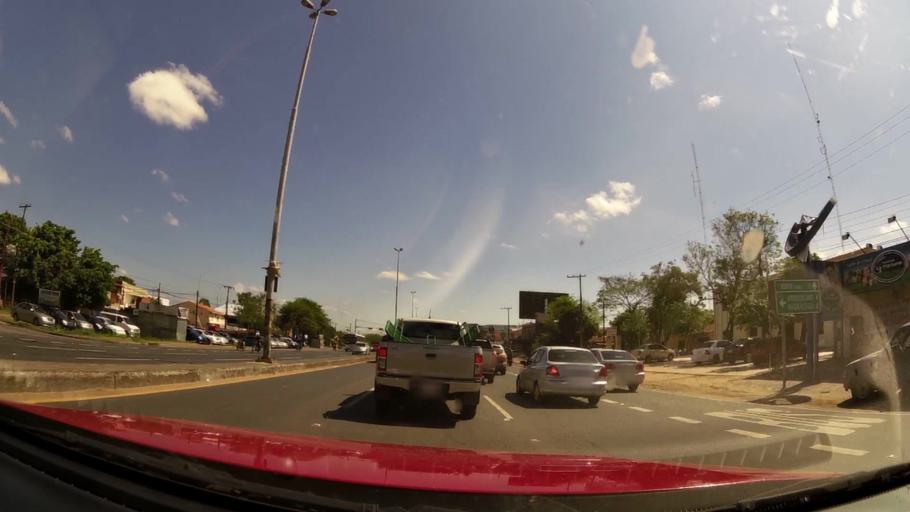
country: PY
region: Central
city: Colonia Mariano Roque Alonso
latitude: -25.2423
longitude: -57.5449
